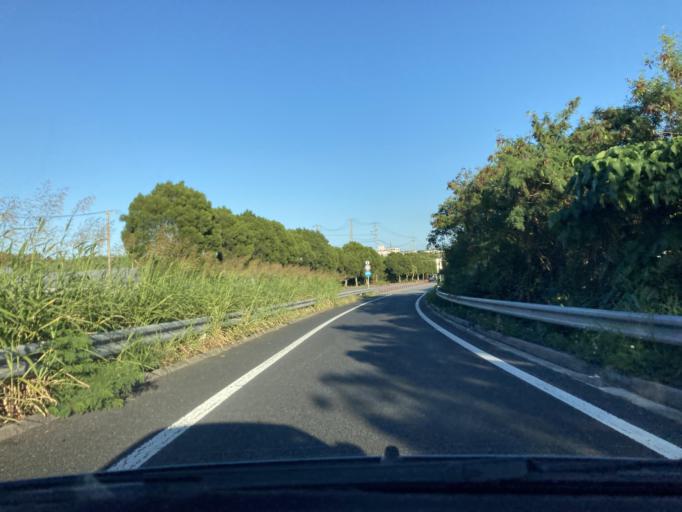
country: JP
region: Okinawa
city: Tomigusuku
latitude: 26.1813
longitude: 127.7210
